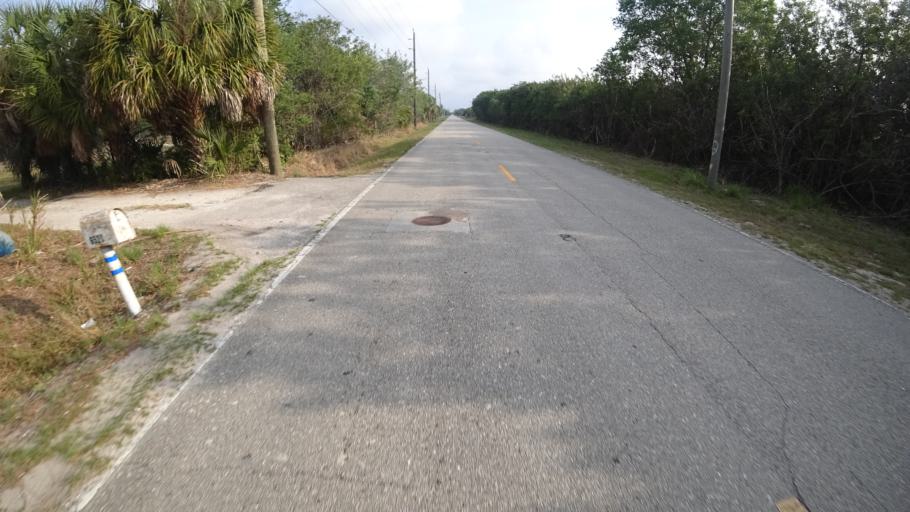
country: US
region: Florida
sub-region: Manatee County
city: Whitfield
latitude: 27.4238
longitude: -82.5219
